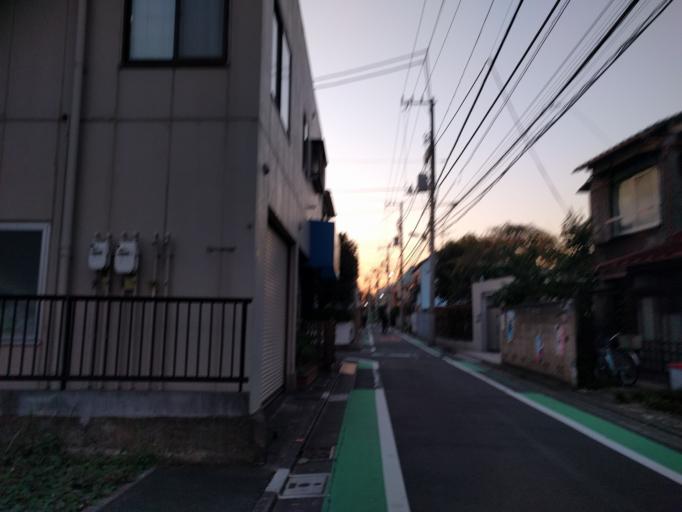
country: JP
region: Tokyo
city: Tokyo
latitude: 35.6434
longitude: 139.6333
